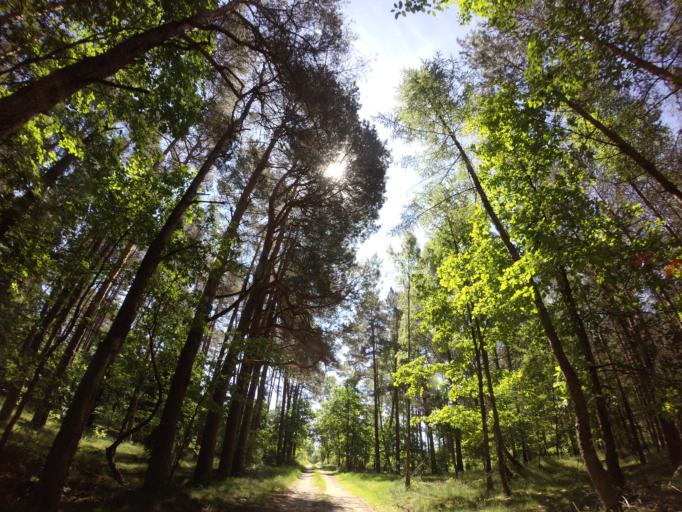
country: PL
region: West Pomeranian Voivodeship
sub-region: Powiat choszczenski
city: Drawno
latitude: 53.2567
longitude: 15.7478
